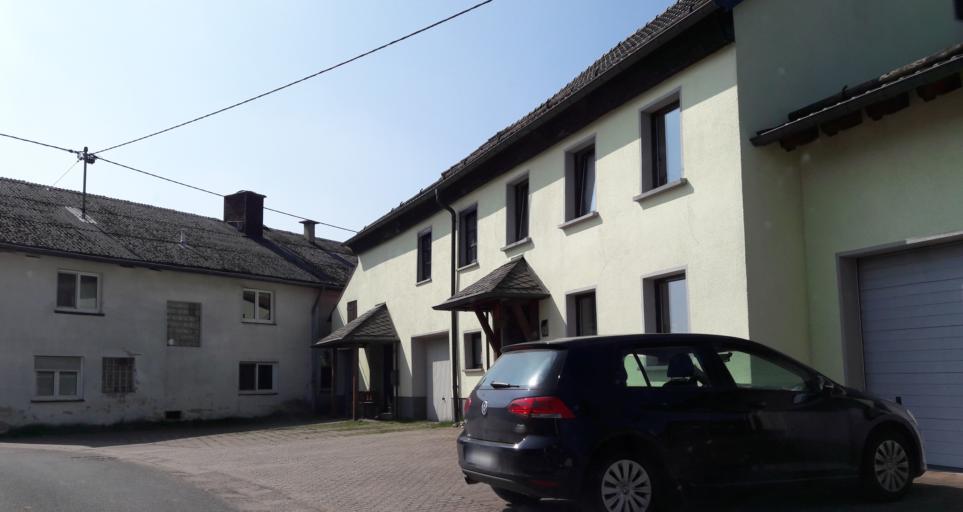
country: DE
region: Saarland
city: Tholey
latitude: 49.5361
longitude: 7.0350
